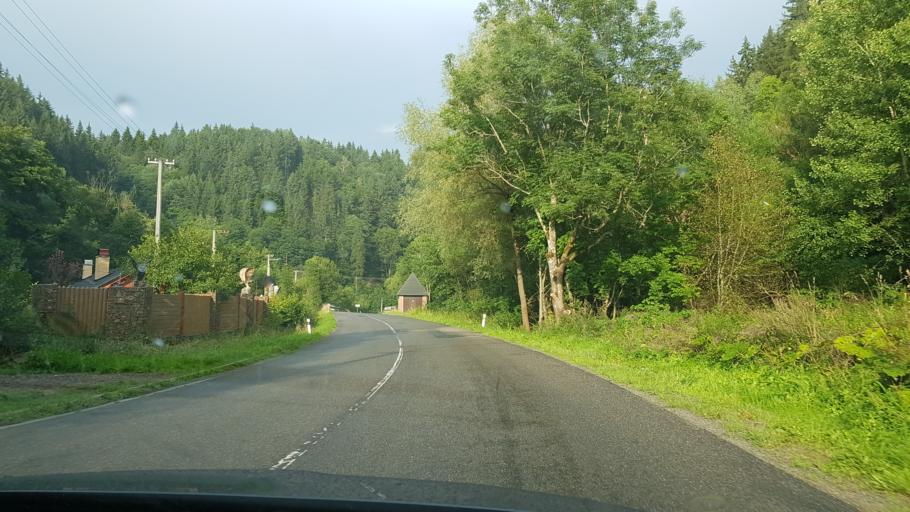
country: CZ
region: Olomoucky
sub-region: Okres Sumperk
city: Hanusovice
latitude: 50.0878
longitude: 16.8997
